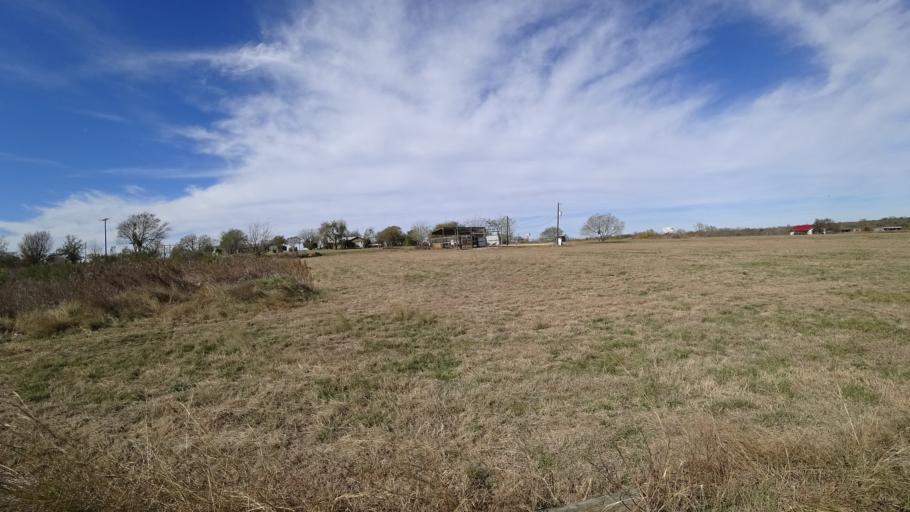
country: US
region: Texas
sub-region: Travis County
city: Onion Creek
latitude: 30.1026
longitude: -97.6935
